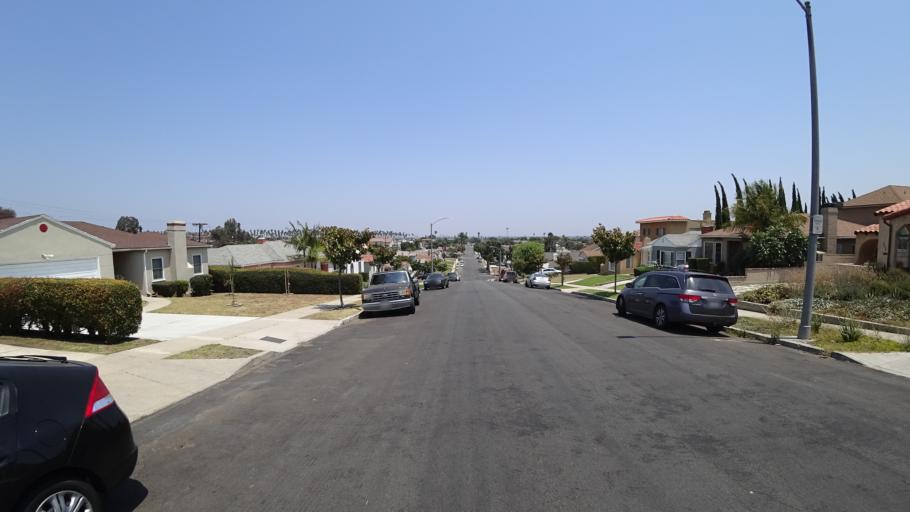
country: US
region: California
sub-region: Los Angeles County
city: View Park-Windsor Hills
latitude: 33.9880
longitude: -118.3490
